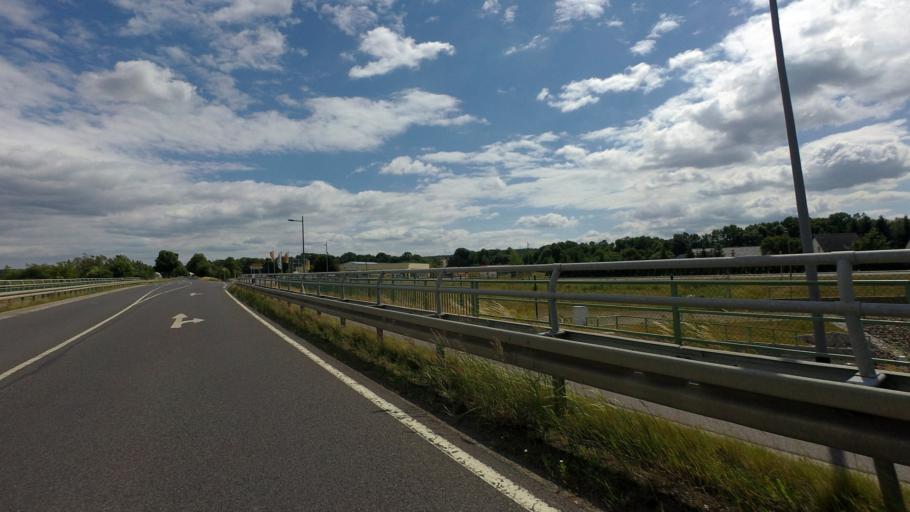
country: DE
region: Brandenburg
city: Senftenberg
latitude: 51.4992
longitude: 14.0646
